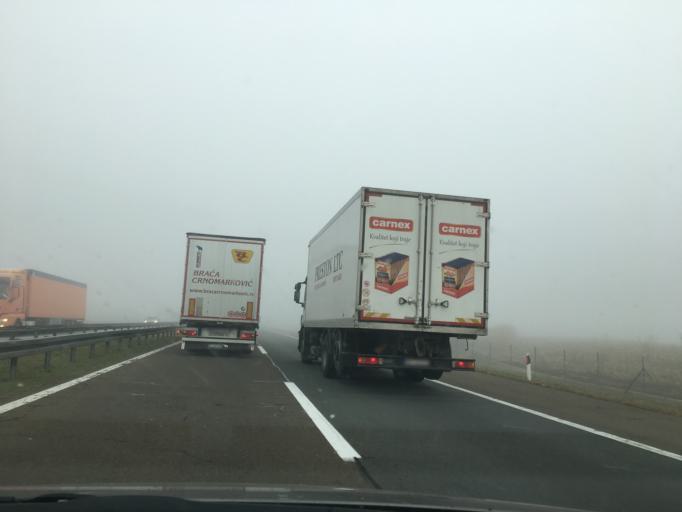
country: RS
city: Novi Karlovci
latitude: 45.0444
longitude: 20.1788
